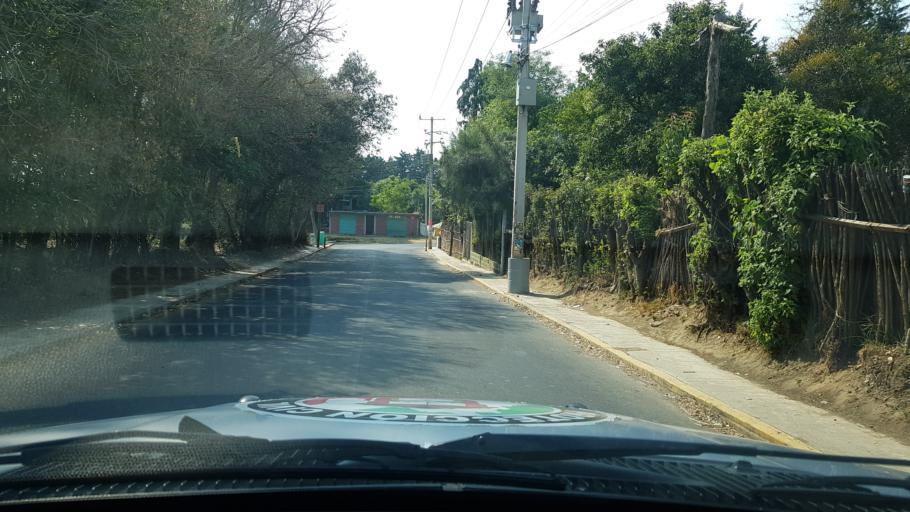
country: MX
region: Mexico
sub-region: Ozumba
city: San Jose Tlacotitlan
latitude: 18.9847
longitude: -98.8108
